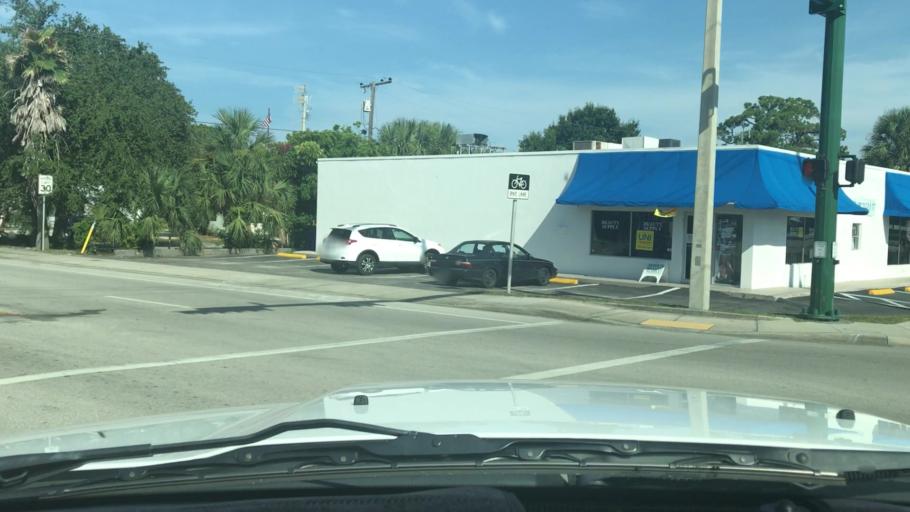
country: US
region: Florida
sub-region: Indian River County
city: Vero Beach
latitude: 27.6316
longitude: -80.3969
